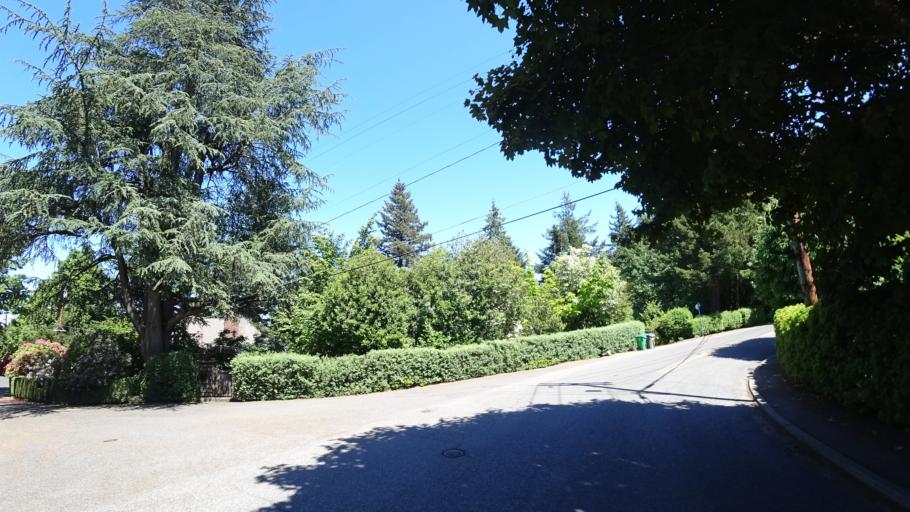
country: US
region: Oregon
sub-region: Multnomah County
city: Portland
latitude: 45.5015
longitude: -122.7113
